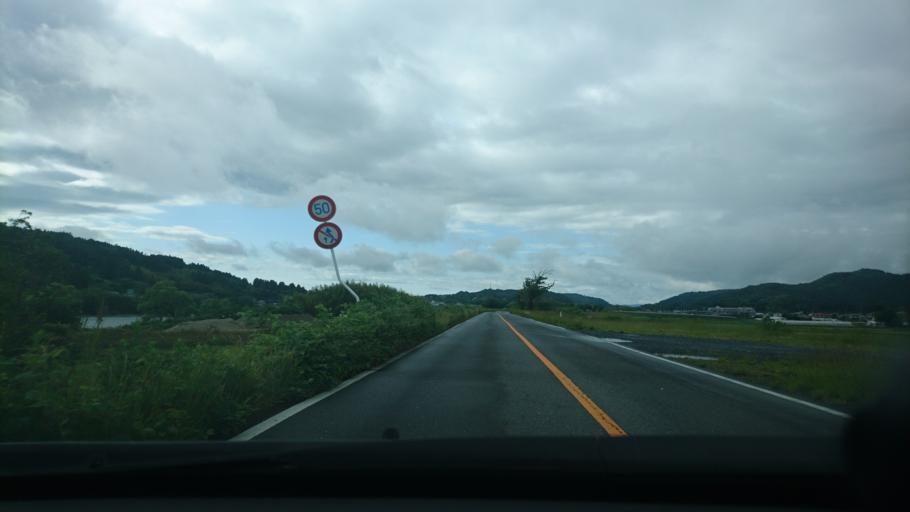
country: JP
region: Miyagi
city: Wakuya
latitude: 38.6420
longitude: 141.2873
